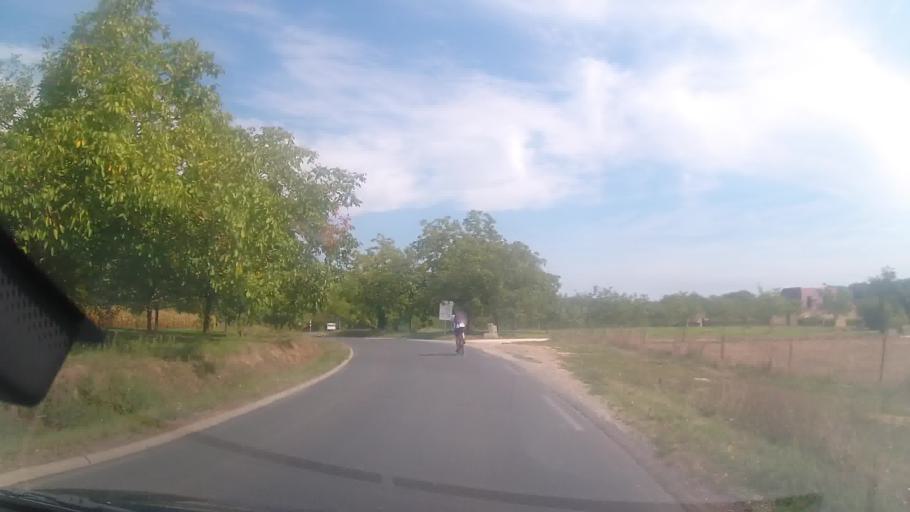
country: FR
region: Aquitaine
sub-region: Departement de la Dordogne
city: Carsac-Aillac
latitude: 44.8358
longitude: 1.2445
